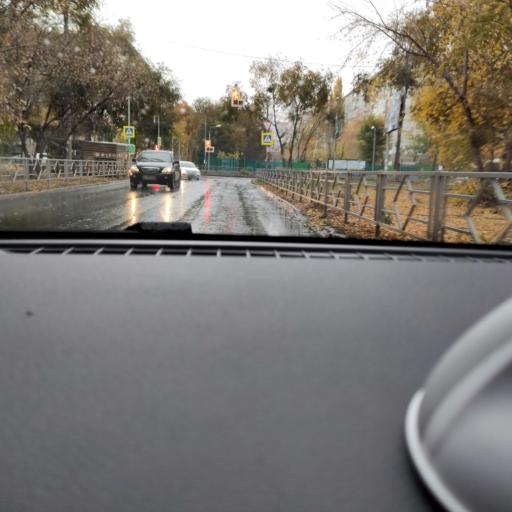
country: RU
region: Samara
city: Samara
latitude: 53.1954
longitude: 50.1359
